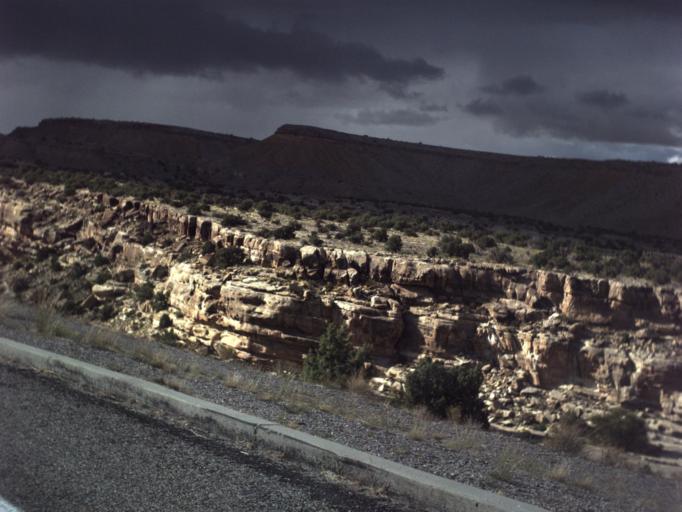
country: US
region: Utah
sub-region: Emery County
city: Castle Dale
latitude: 38.9401
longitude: -110.4819
